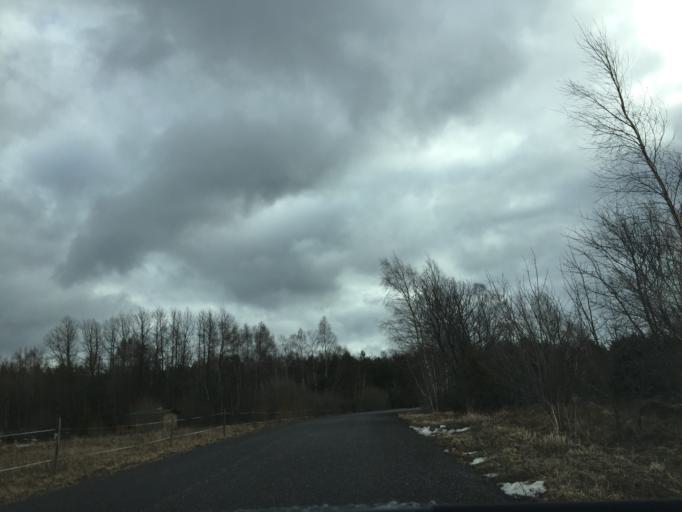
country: EE
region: Laeaene
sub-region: Ridala Parish
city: Uuemoisa
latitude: 58.6748
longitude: 23.5539
